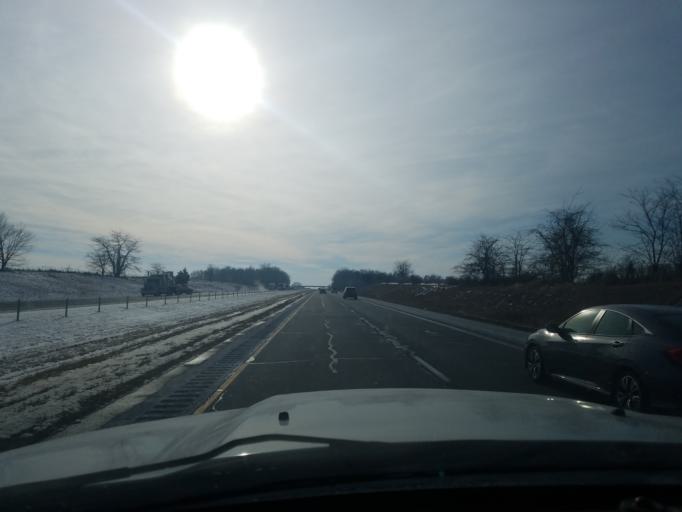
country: US
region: Indiana
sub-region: Huntington County
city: Warren
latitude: 40.7043
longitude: -85.4571
